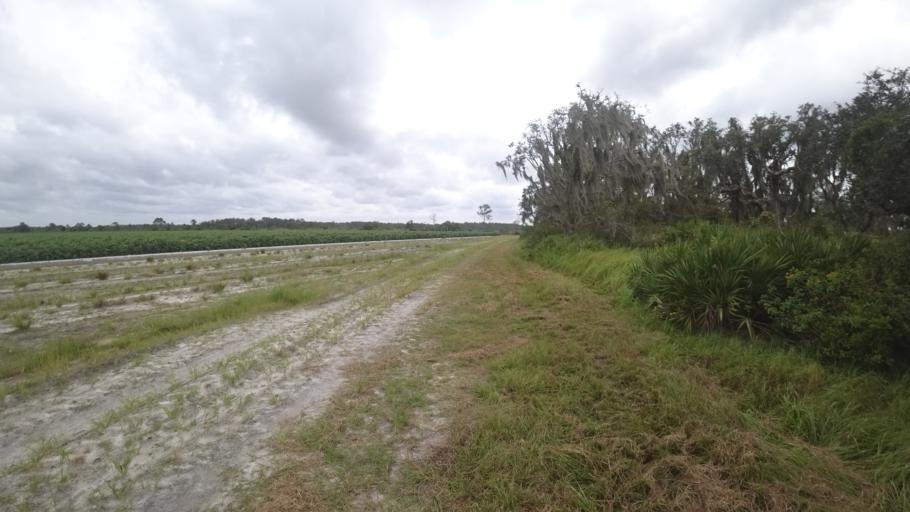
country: US
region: Florida
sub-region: Hillsborough County
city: Wimauma
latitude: 27.5607
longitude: -82.1341
